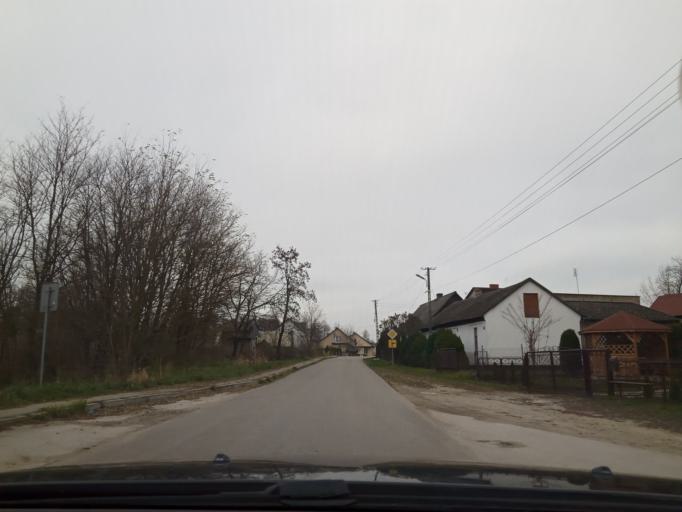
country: PL
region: Swietokrzyskie
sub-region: Powiat jedrzejowski
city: Imielno
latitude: 50.5879
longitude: 20.4765
